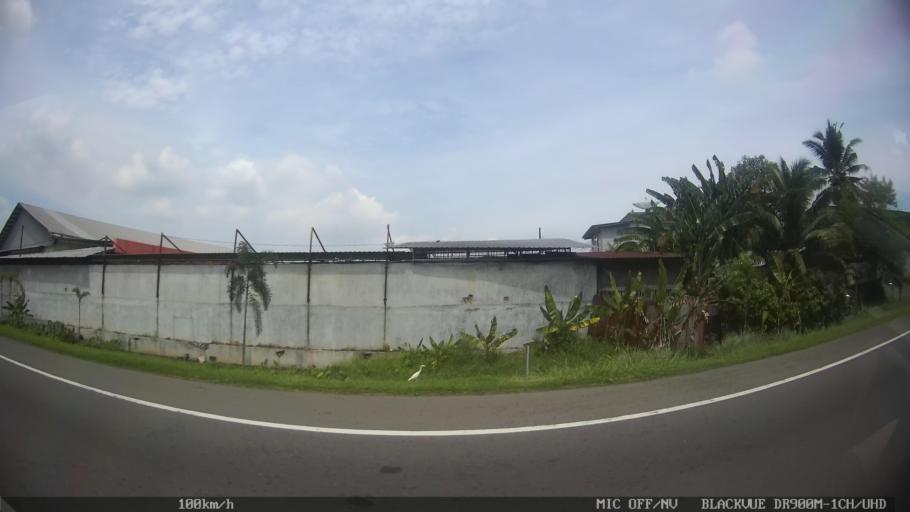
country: ID
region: North Sumatra
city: Labuhan Deli
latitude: 3.7052
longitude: 98.6815
